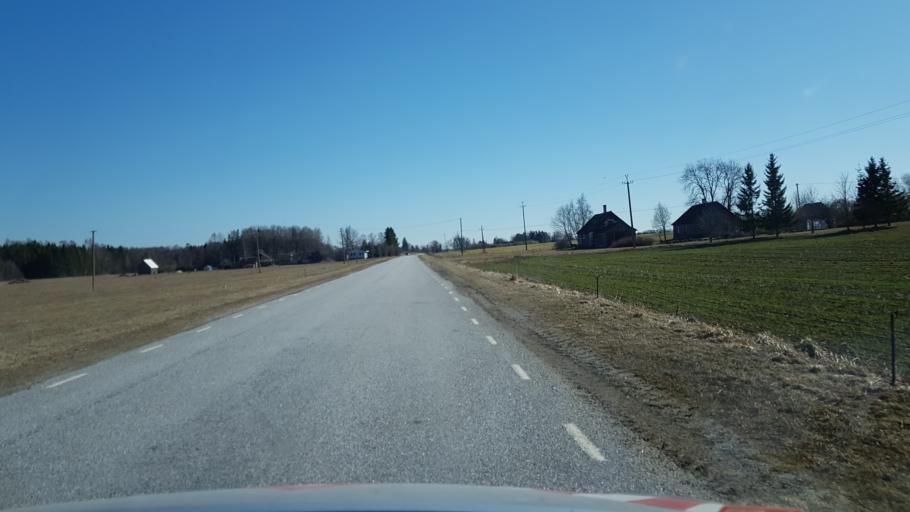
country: EE
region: Jaervamaa
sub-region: Koeru vald
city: Koeru
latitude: 59.0467
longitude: 26.0895
